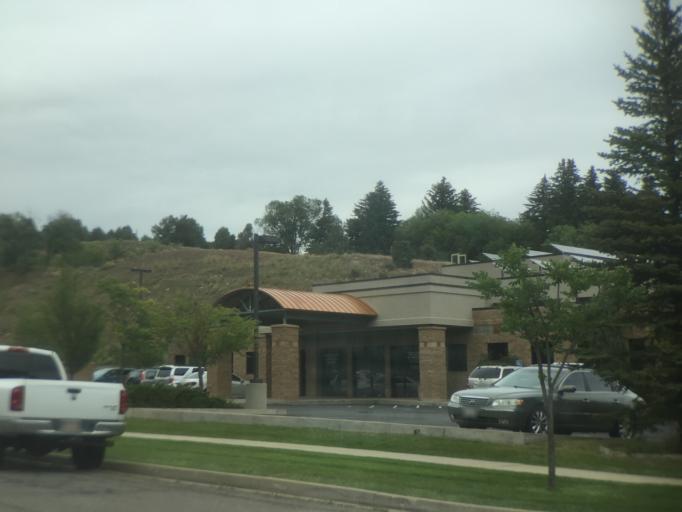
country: US
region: Colorado
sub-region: La Plata County
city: Durango
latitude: 37.2727
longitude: -107.8921
